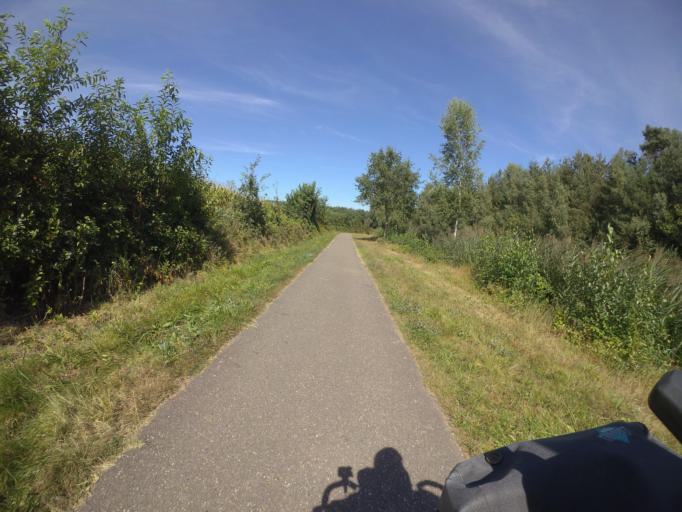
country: NL
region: Overijssel
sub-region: Gemeente Twenterand
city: Den Ham
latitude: 52.4153
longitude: 6.4096
